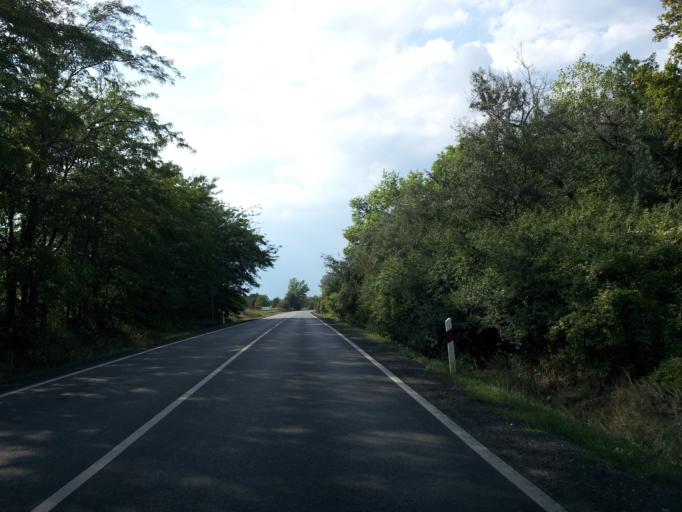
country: HU
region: Pest
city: Vac
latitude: 47.8044
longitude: 19.1002
